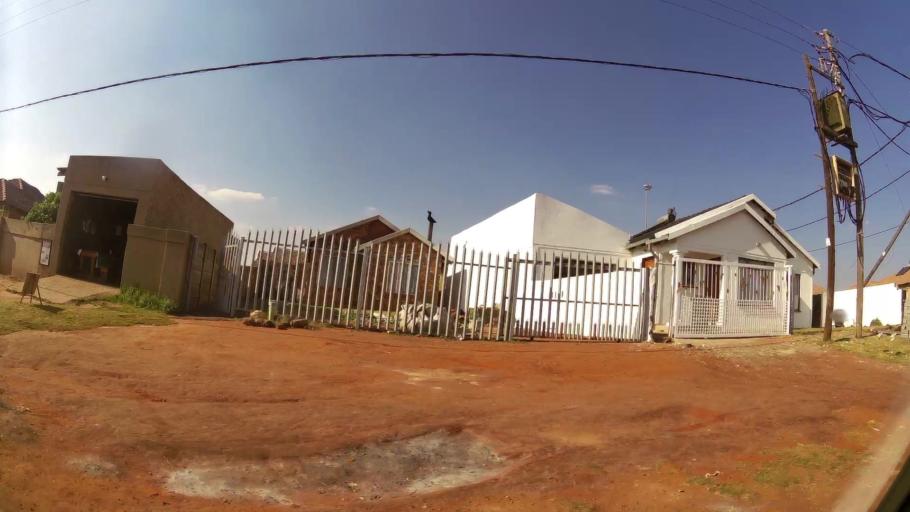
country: ZA
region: Gauteng
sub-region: Ekurhuleni Metropolitan Municipality
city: Benoni
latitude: -26.2288
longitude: 28.3232
